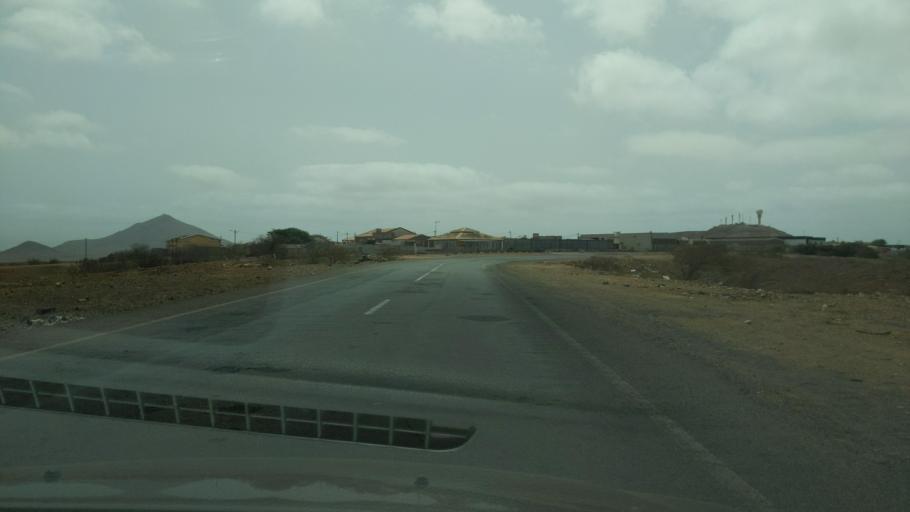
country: CV
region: Sal
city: Espargos
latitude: 16.7602
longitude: -22.9563
